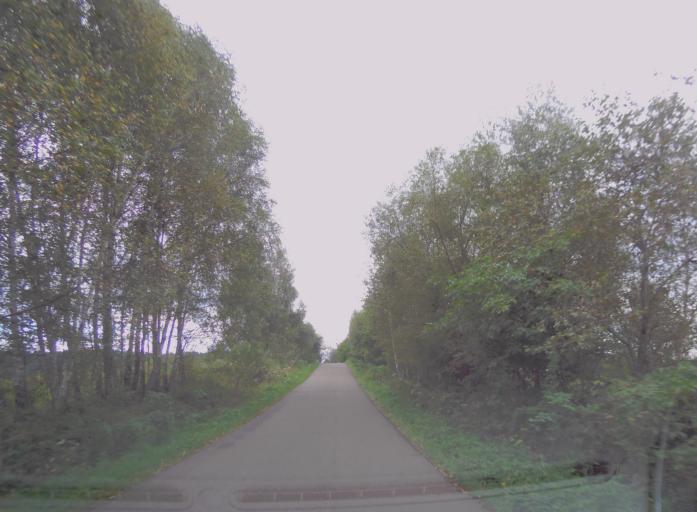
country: PL
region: Subcarpathian Voivodeship
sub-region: Powiat leski
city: Polanczyk
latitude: 49.2973
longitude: 22.5091
